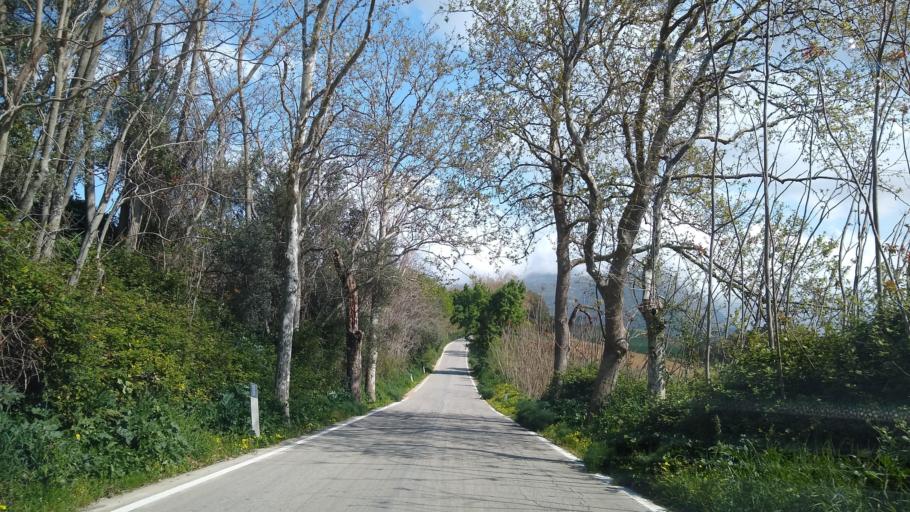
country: IT
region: Sicily
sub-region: Trapani
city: Calatafimi
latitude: 37.9371
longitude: 12.8506
